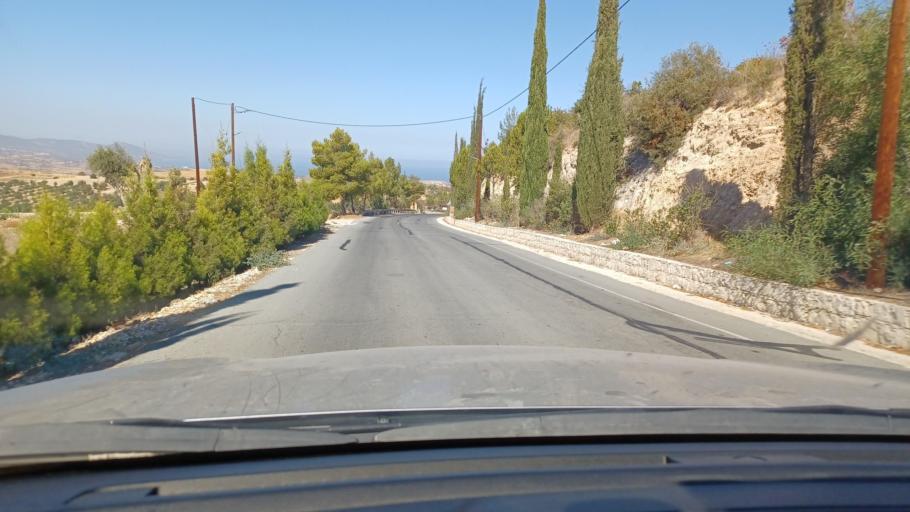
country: CY
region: Pafos
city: Polis
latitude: 34.9886
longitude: 32.4800
